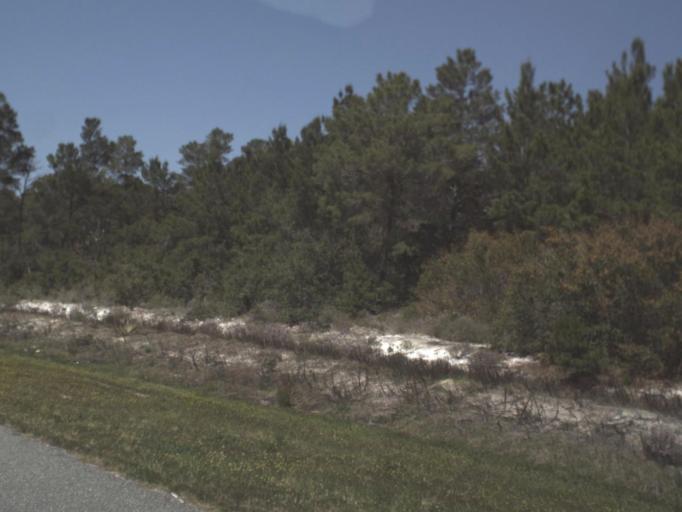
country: US
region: Florida
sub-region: Gulf County
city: Port Saint Joe
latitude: 29.8882
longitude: -85.3493
